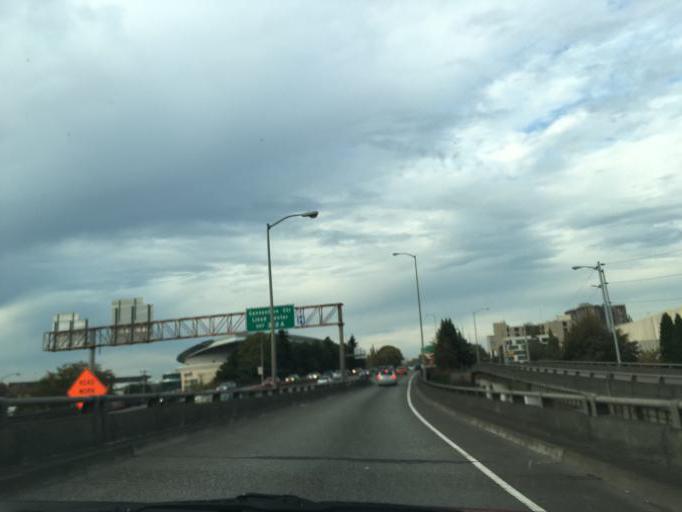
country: US
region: Oregon
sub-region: Multnomah County
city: Portland
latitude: 45.5275
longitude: -122.6649
